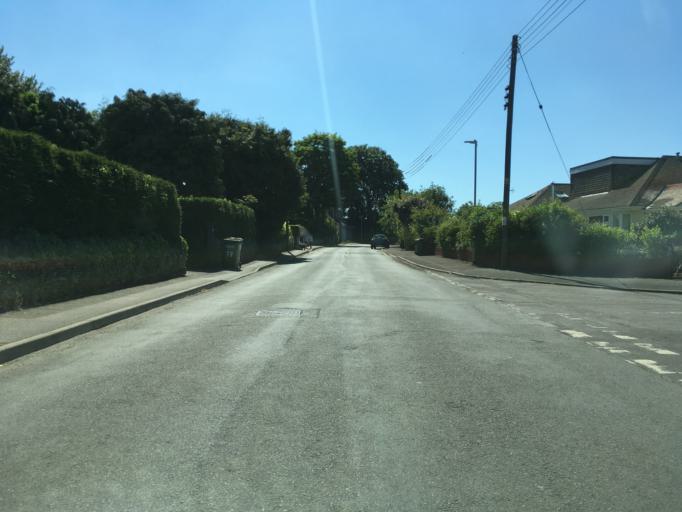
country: GB
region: England
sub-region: South Gloucestershire
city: Winterbourne
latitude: 51.5350
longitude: -2.4900
